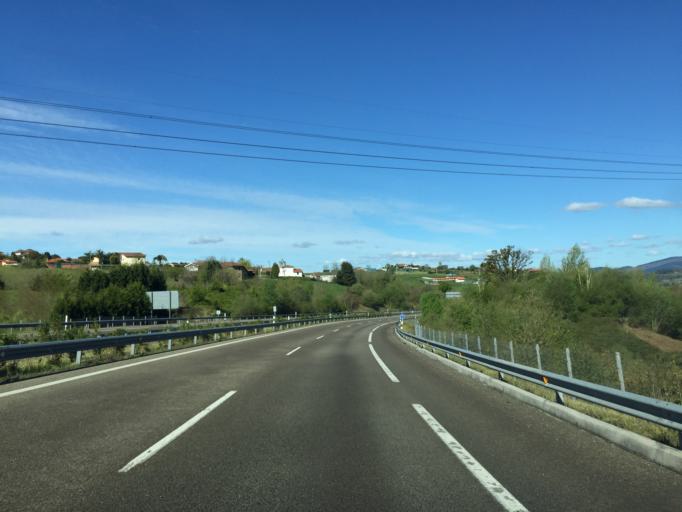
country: ES
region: Asturias
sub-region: Province of Asturias
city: Oviedo
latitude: 43.3479
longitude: -5.9033
